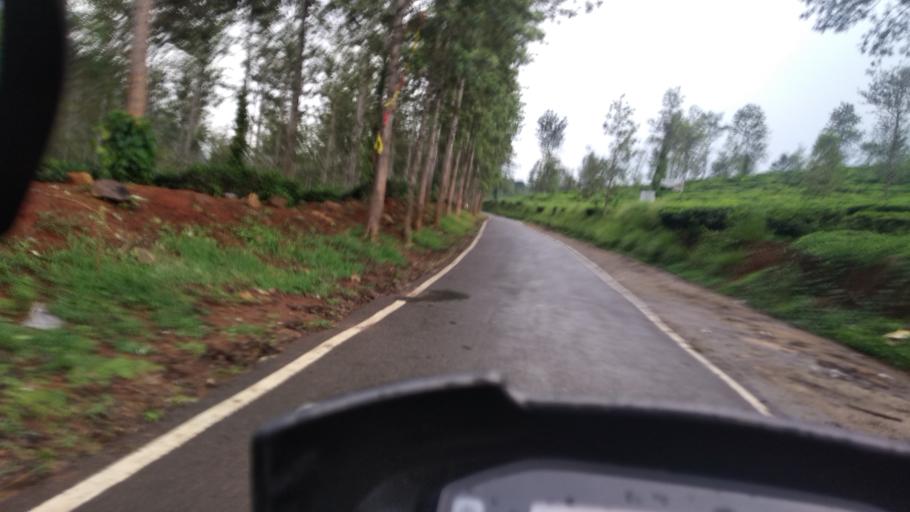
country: IN
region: Tamil Nadu
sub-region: Theni
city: Gudalur
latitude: 9.5689
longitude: 77.0854
